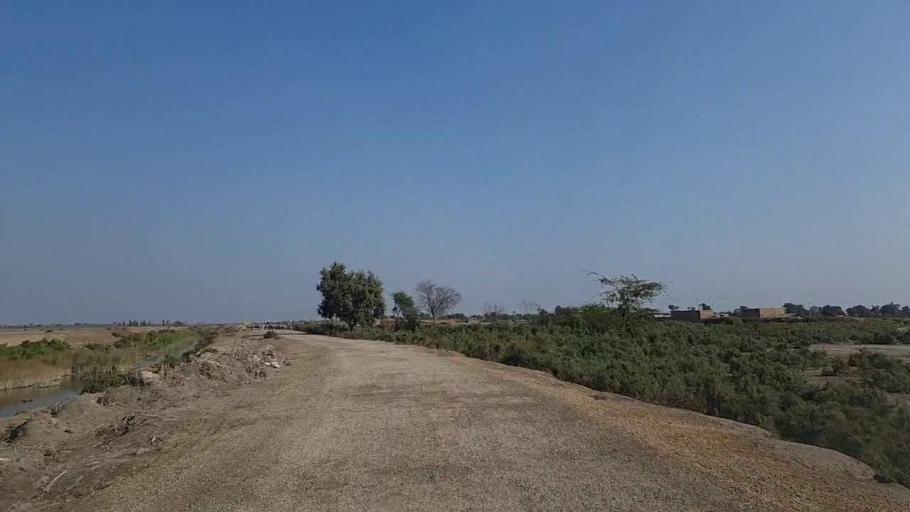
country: PK
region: Sindh
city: Jam Sahib
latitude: 26.2870
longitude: 68.6019
